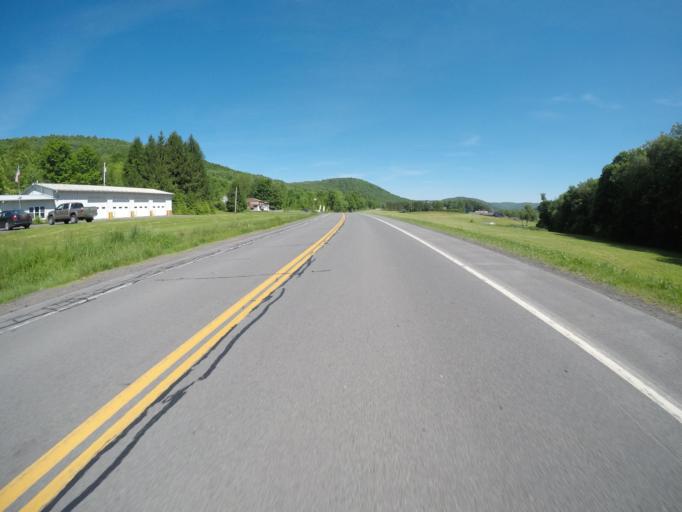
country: US
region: New York
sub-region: Delaware County
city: Delhi
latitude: 42.2209
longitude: -74.9678
